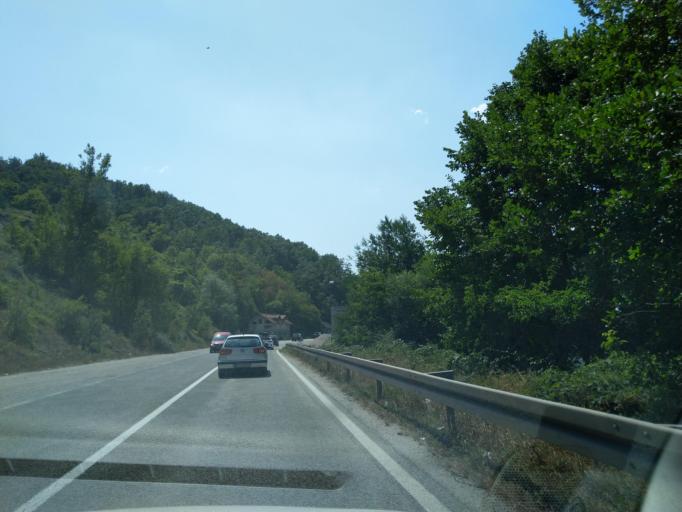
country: RS
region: Central Serbia
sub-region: Zlatiborski Okrug
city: Prijepolje
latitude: 43.4505
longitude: 19.6422
